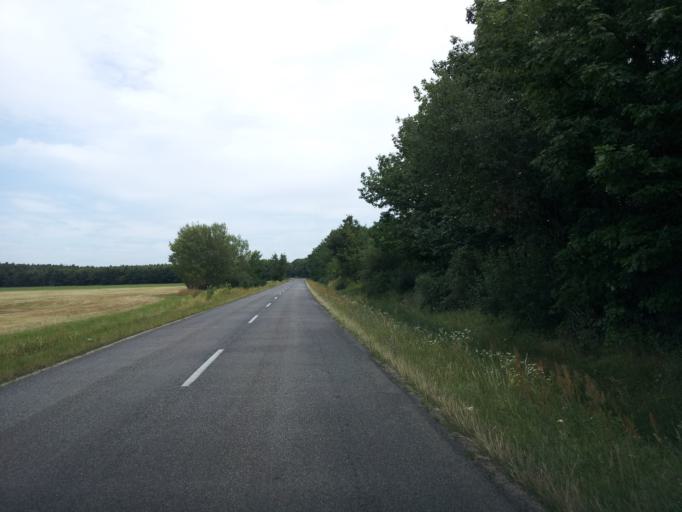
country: HU
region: Vas
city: Vasvar
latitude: 47.0469
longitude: 16.8336
